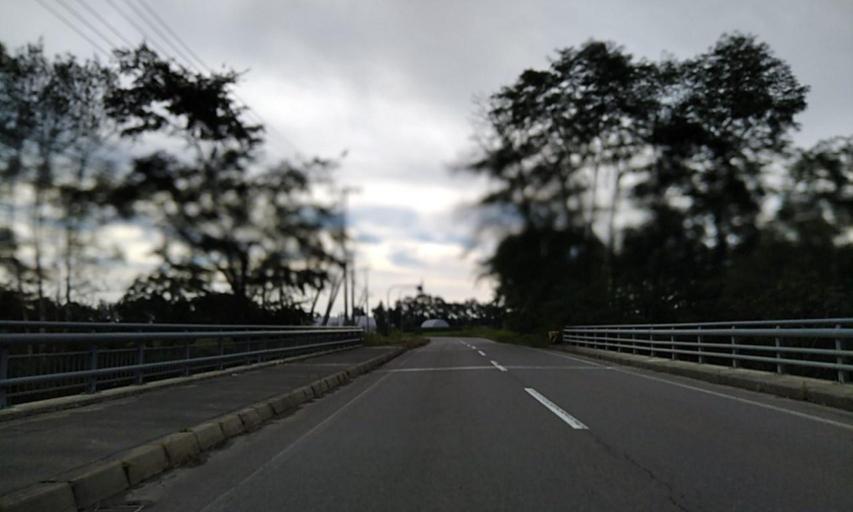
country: JP
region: Hokkaido
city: Obihiro
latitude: 42.8560
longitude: 143.1516
